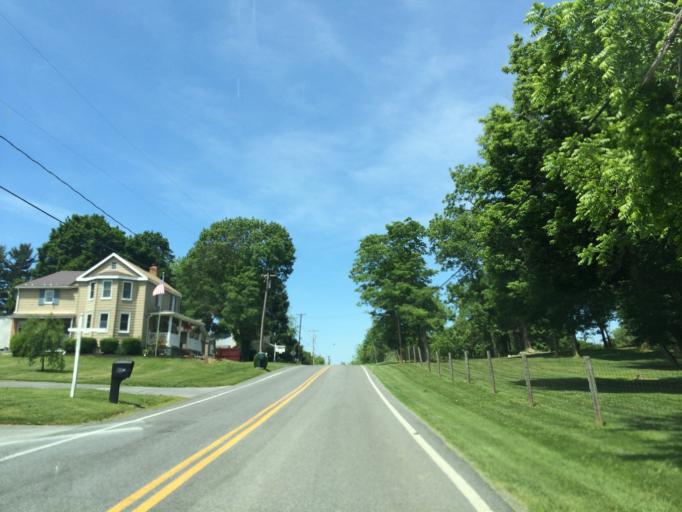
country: US
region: Maryland
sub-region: Washington County
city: Saint James
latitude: 39.5376
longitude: -77.7335
